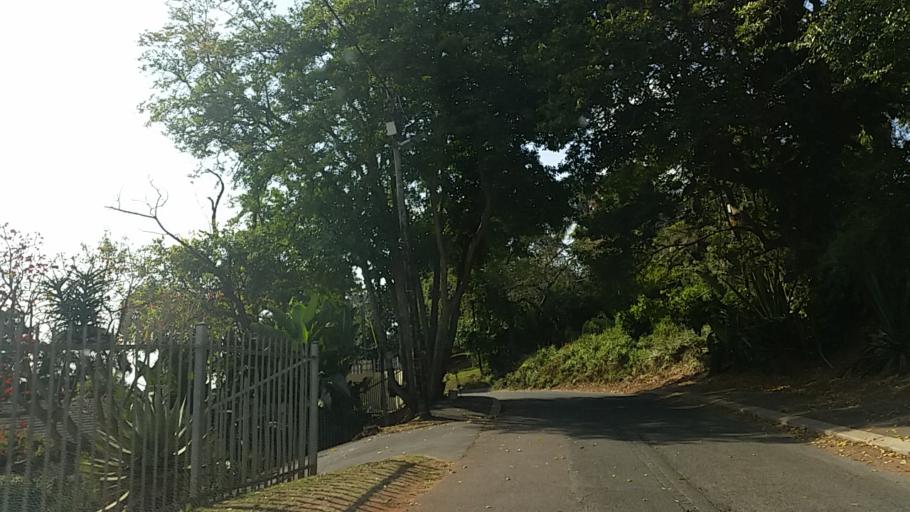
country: ZA
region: KwaZulu-Natal
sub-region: eThekwini Metropolitan Municipality
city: Berea
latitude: -29.8350
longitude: 30.9064
